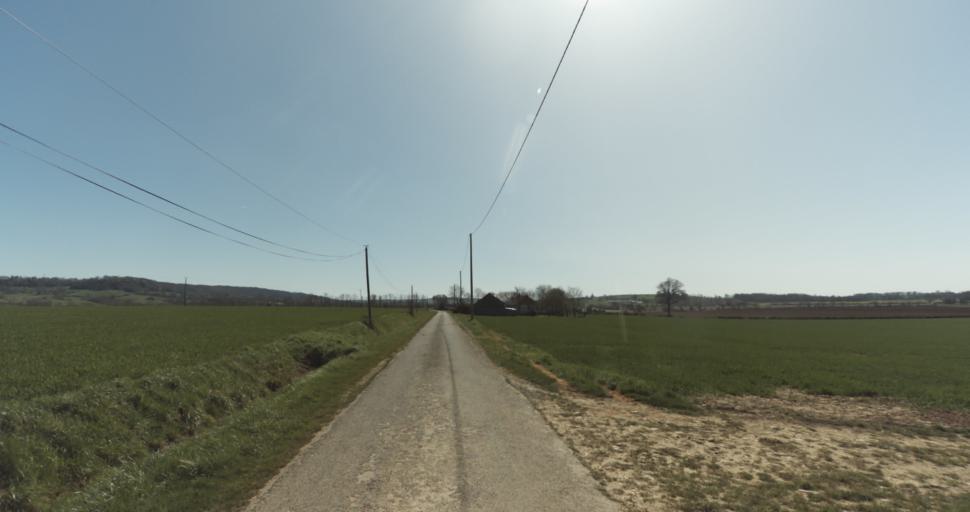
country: FR
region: Lower Normandy
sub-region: Departement du Calvados
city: Saint-Pierre-sur-Dives
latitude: 49.0044
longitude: 0.0199
